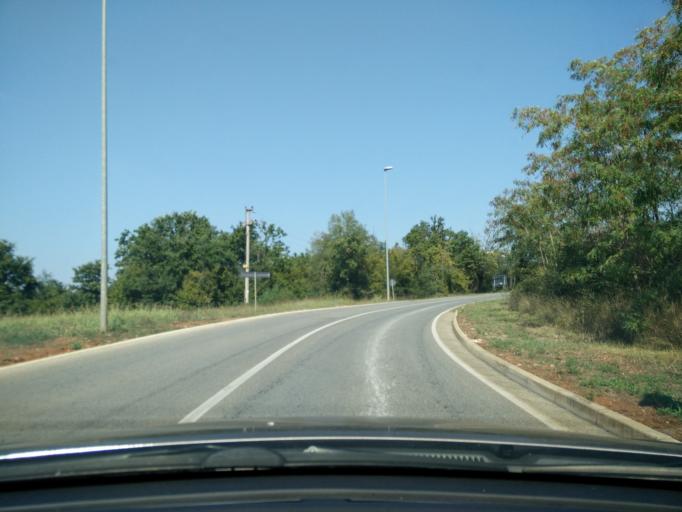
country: HR
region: Istarska
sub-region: Grad Porec
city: Porec
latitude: 45.2600
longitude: 13.6307
